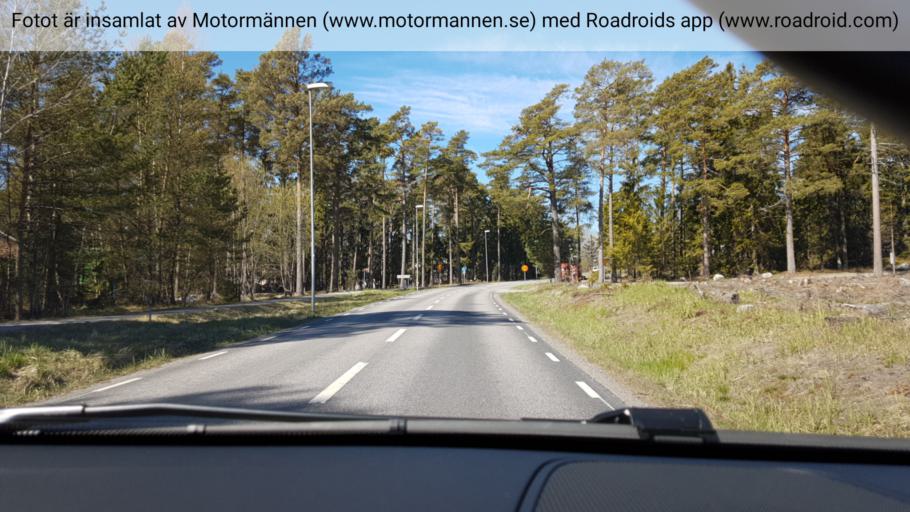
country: SE
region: Stockholm
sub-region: Varmdo Kommun
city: Holo
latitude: 59.2864
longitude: 18.6953
